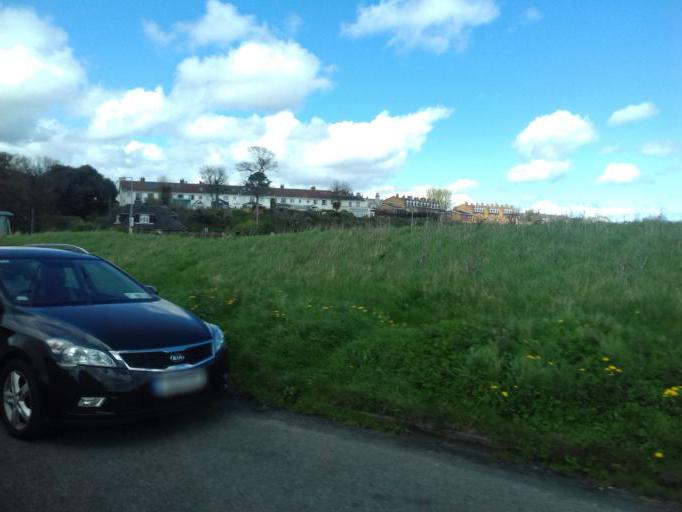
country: IE
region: Leinster
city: Dollymount
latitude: 53.3736
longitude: -6.1635
